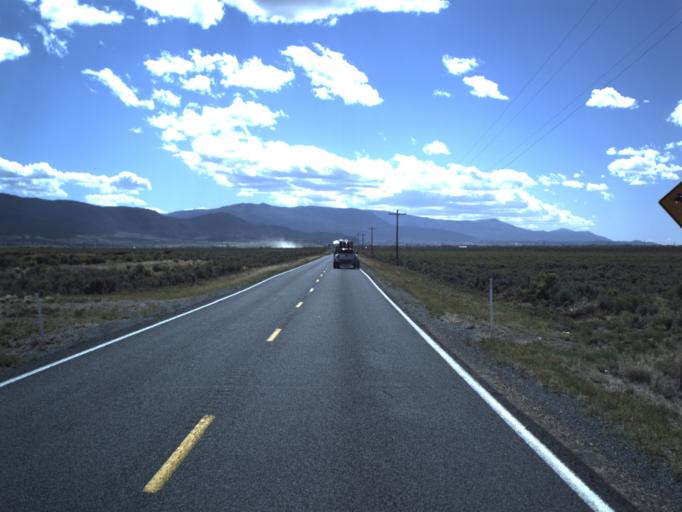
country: US
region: Utah
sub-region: Iron County
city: Enoch
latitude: 37.8307
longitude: -113.0504
